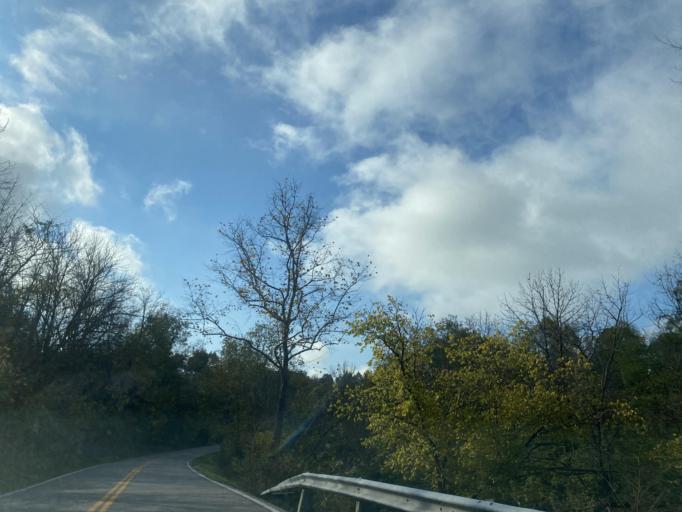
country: US
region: Kentucky
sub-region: Pendleton County
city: Falmouth
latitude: 38.7168
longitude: -84.3016
